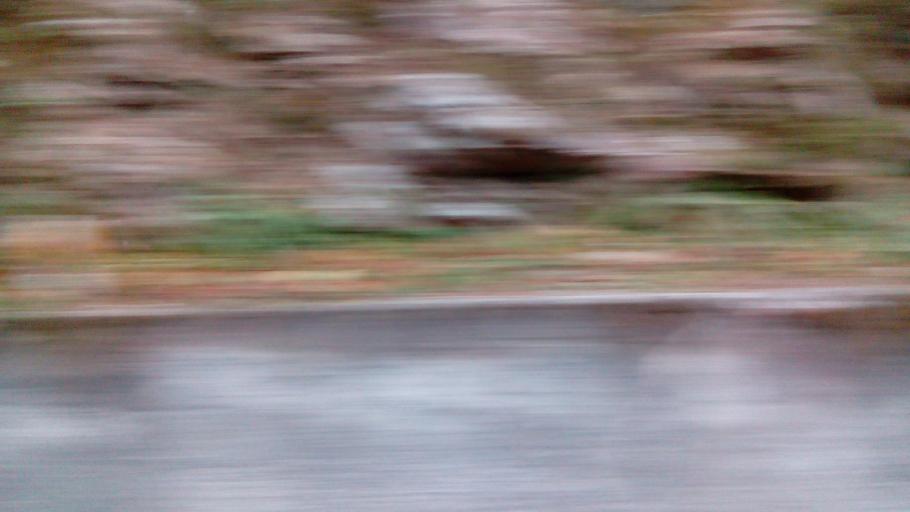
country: TW
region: Taiwan
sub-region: Hualien
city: Hualian
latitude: 24.3838
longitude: 121.3471
